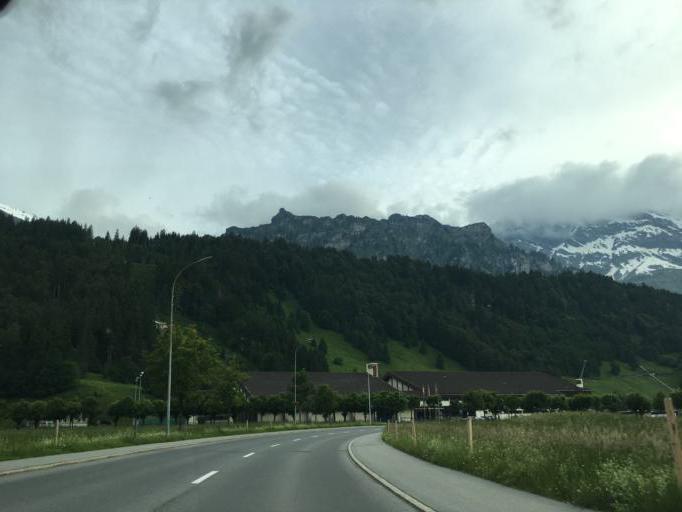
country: CH
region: Obwalden
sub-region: Obwalden
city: Engelberg
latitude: 46.8191
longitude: 8.4065
